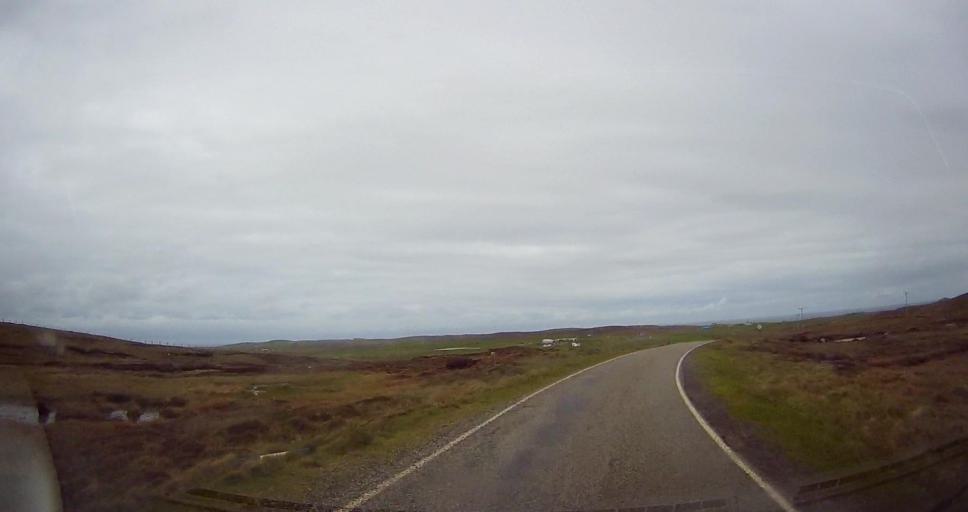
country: GB
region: Scotland
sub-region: Shetland Islands
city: Lerwick
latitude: 60.4871
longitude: -1.5353
